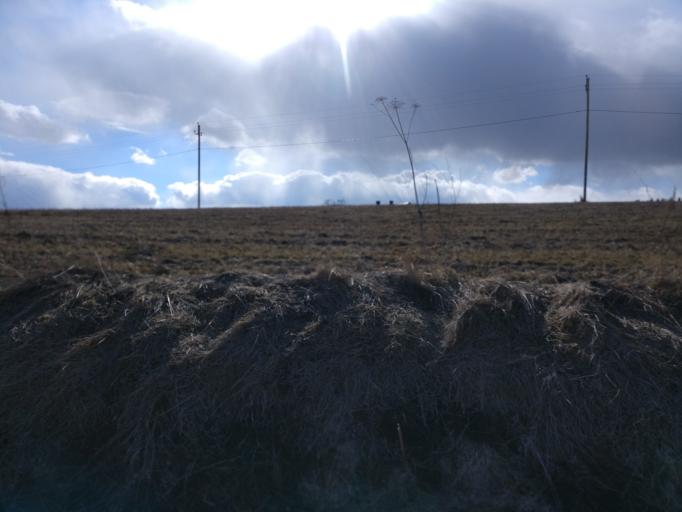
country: FI
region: Uusimaa
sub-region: Helsinki
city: Karjalohja
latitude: 60.2712
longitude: 23.6624
